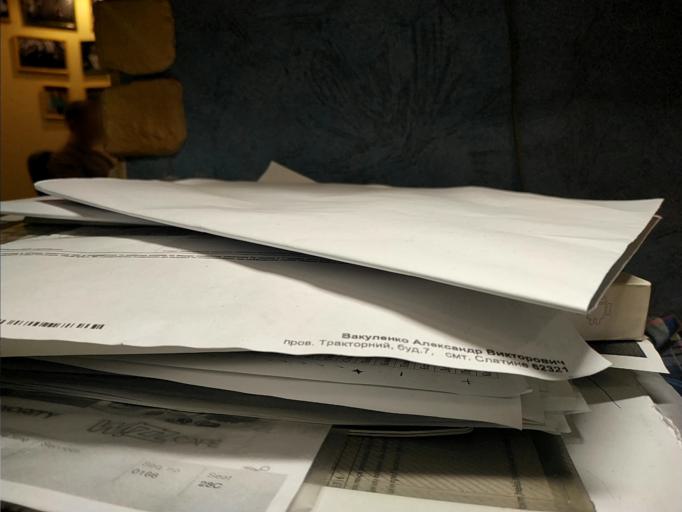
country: RU
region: Tverskaya
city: Zubtsov
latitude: 56.1070
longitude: 34.6486
